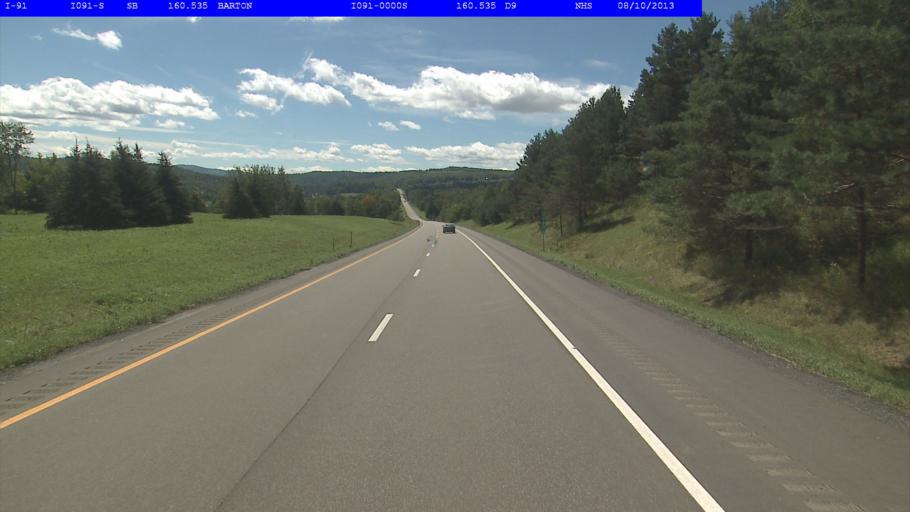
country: US
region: Vermont
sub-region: Orleans County
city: Newport
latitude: 44.7943
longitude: -72.2167
